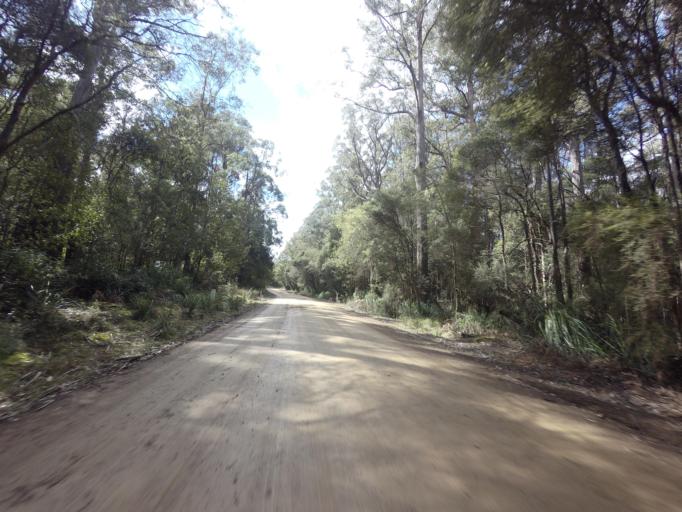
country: AU
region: Tasmania
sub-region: Huon Valley
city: Geeveston
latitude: -43.4155
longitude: 146.8896
